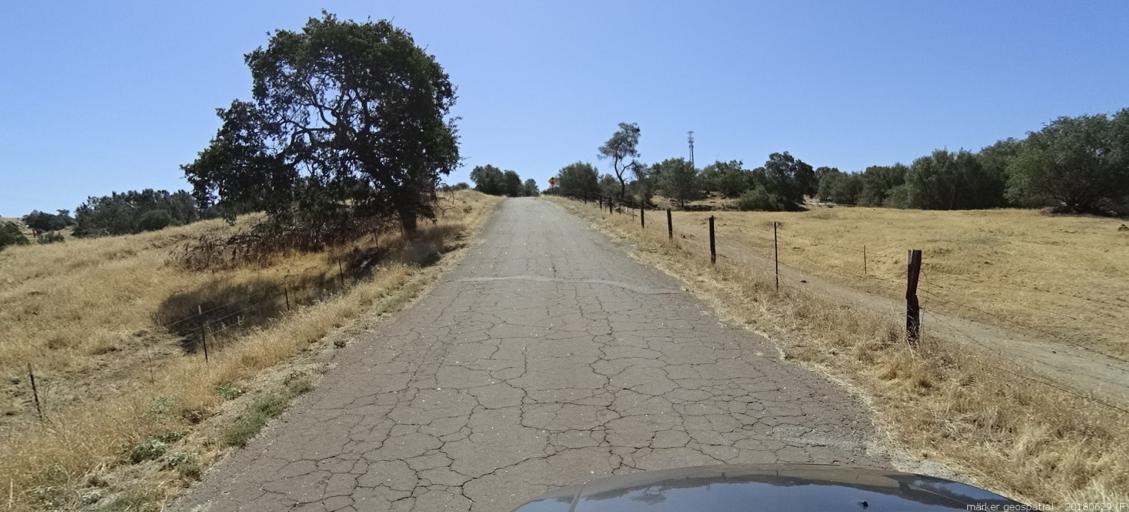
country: US
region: California
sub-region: Madera County
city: Yosemite Lakes
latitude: 37.0954
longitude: -119.7549
